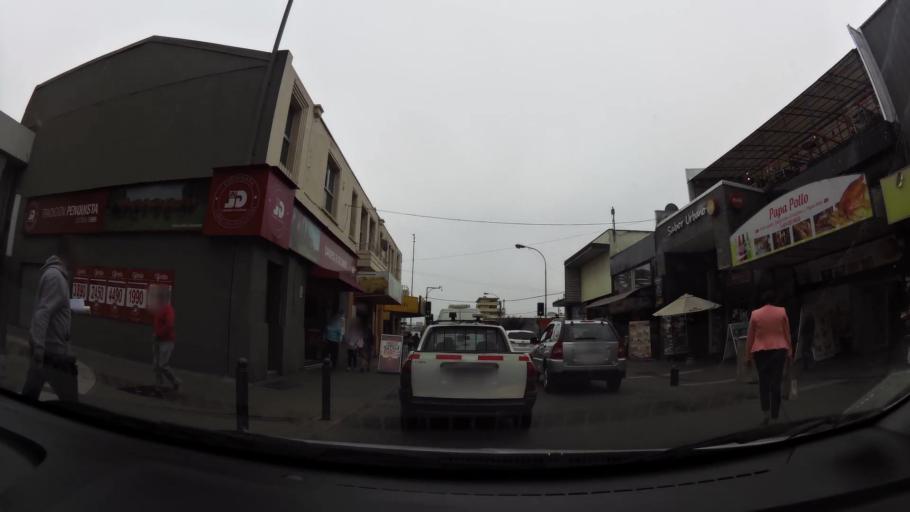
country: CL
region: Biobio
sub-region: Provincia de Concepcion
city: Concepcion
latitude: -36.8262
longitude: -73.0516
